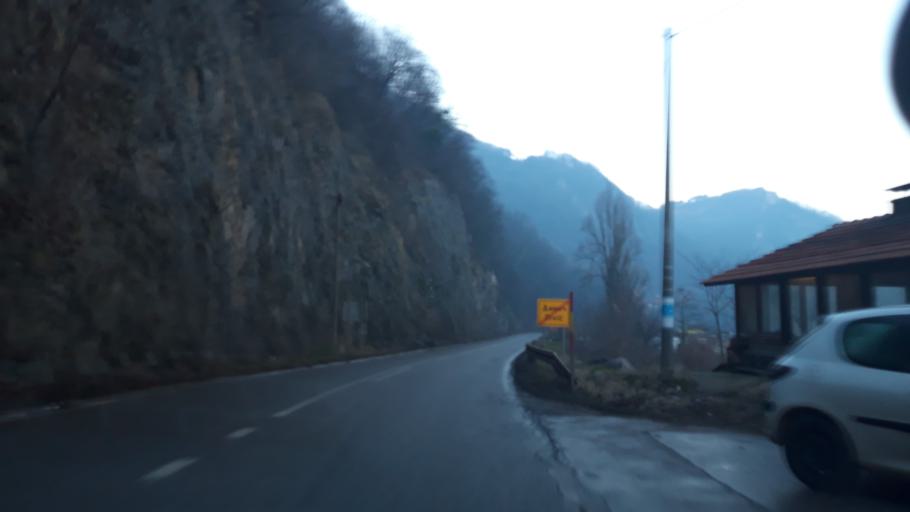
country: RS
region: Central Serbia
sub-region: Macvanski Okrug
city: Mali Zvornik
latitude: 44.3654
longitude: 19.1065
